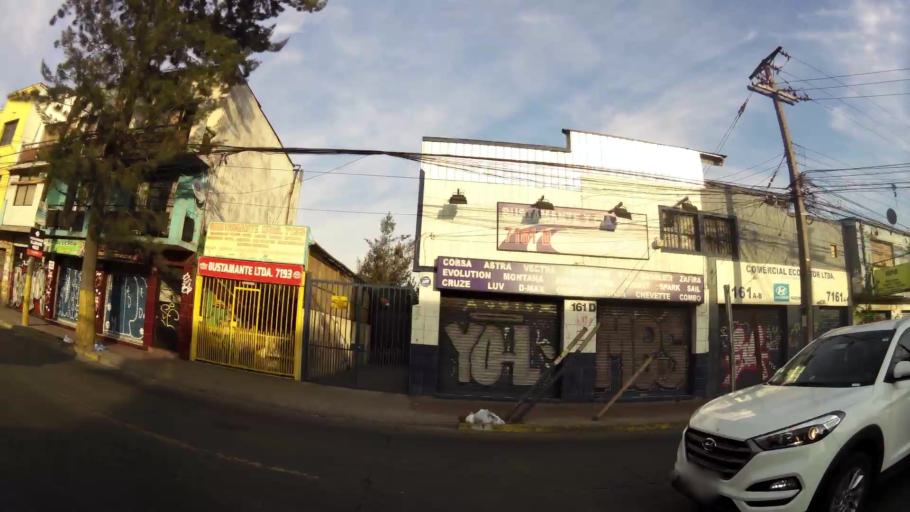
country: CL
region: Santiago Metropolitan
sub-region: Provincia de Santiago
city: Santiago
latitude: -33.5219
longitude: -70.6603
